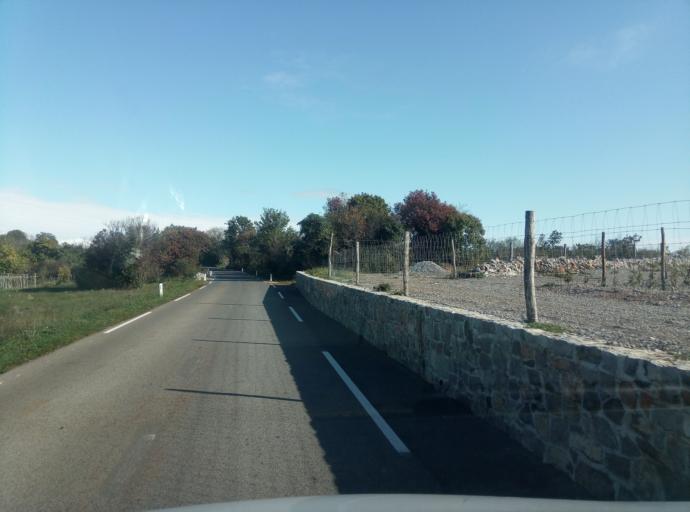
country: SI
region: Komen
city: Komen
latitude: 45.8061
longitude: 13.7199
